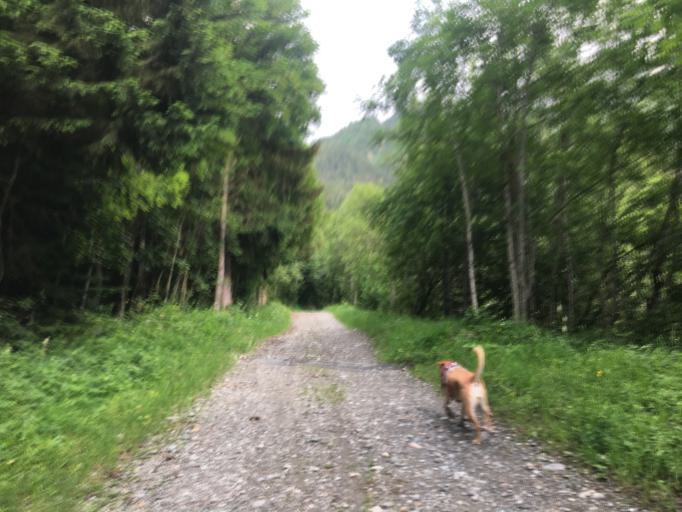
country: FR
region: Rhone-Alpes
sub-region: Departement de la Haute-Savoie
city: Les Houches
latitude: 45.8874
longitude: 6.8077
